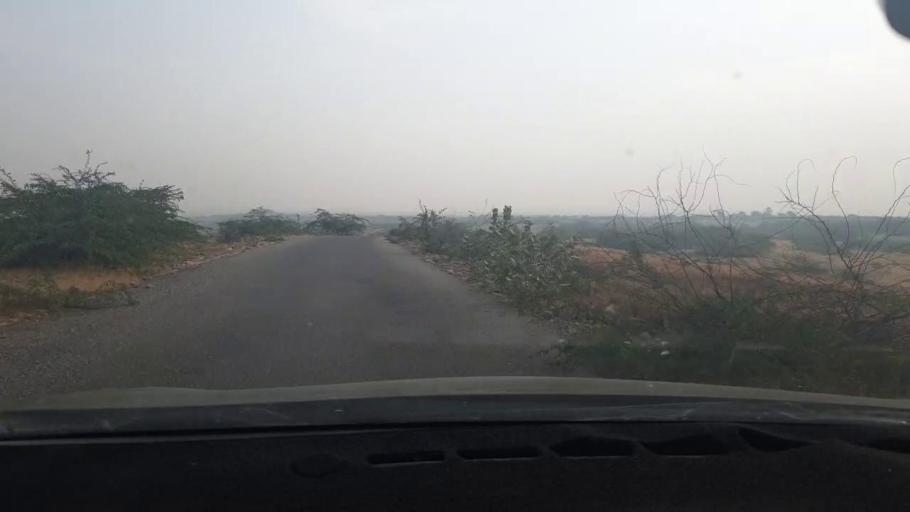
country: PK
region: Sindh
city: Malir Cantonment
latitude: 24.9516
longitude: 67.4337
